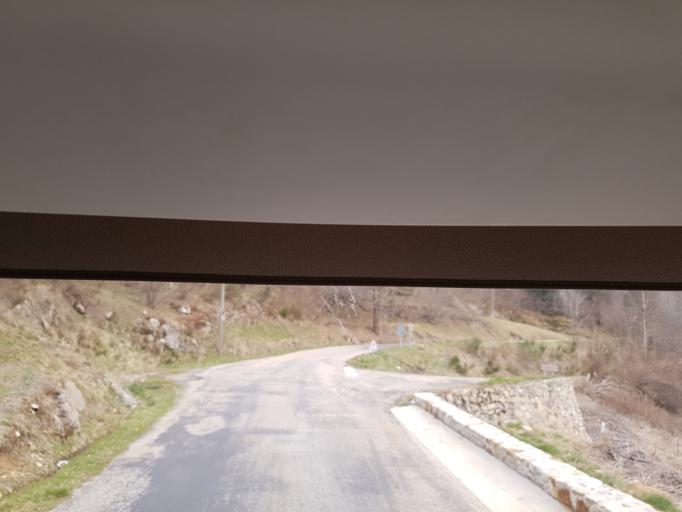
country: FR
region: Languedoc-Roussillon
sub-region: Departement de l'Aude
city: Quillan
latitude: 42.6908
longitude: 2.1008
